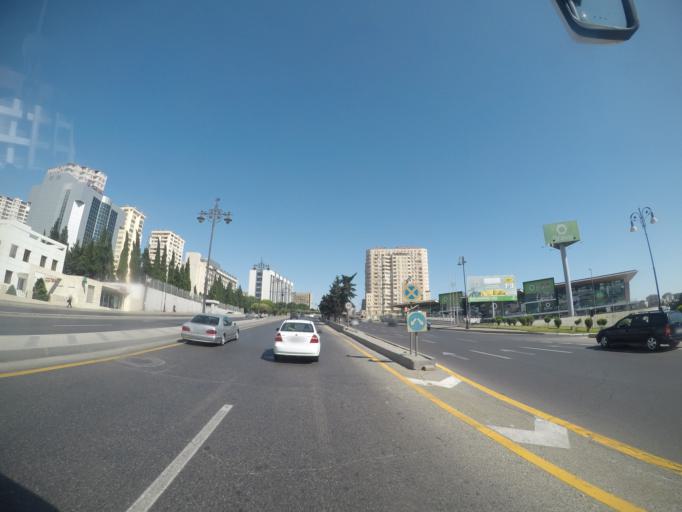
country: AZ
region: Baki
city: Khodzhi-Gasan
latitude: 40.4001
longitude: 49.8110
